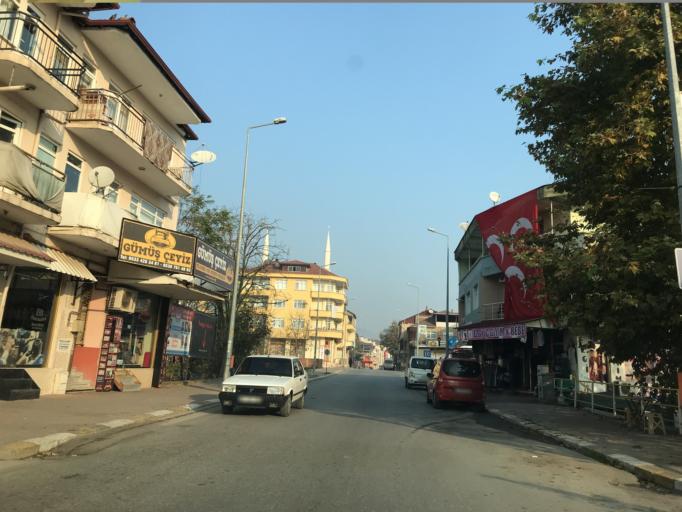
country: TR
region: Duzce
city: Cumayeri
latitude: 40.8746
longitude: 30.9504
